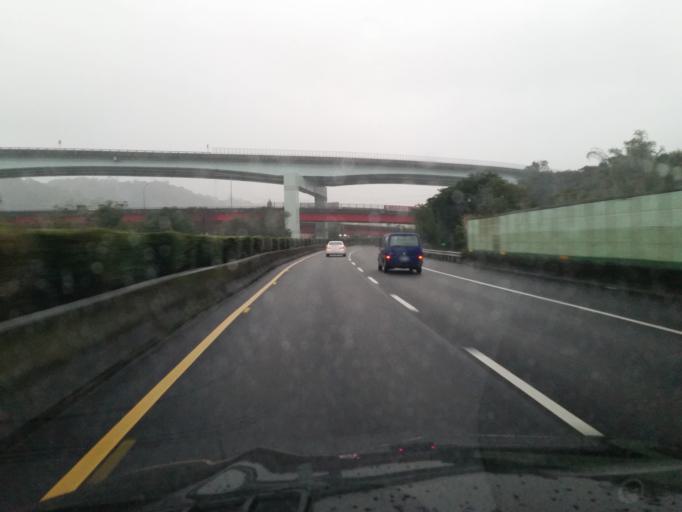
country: TW
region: Taiwan
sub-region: Keelung
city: Keelung
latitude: 25.1069
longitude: 121.7248
